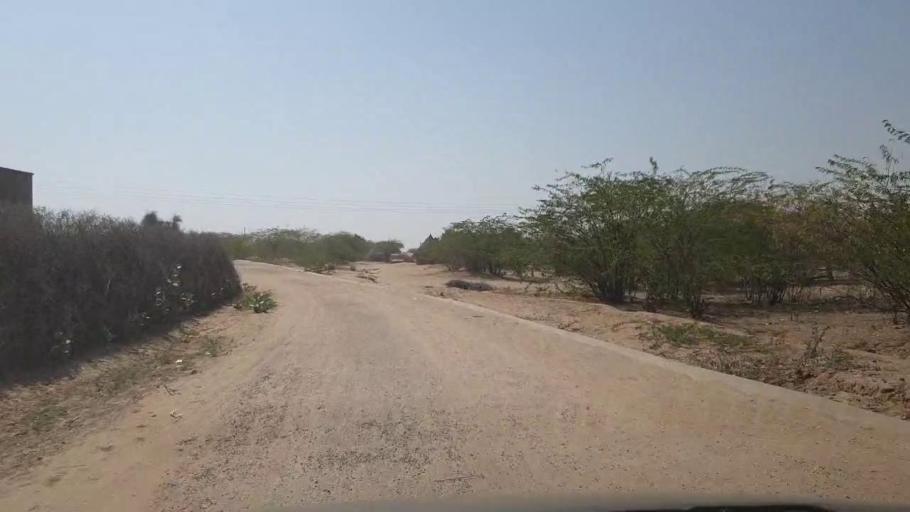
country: PK
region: Sindh
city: Chor
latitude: 25.5649
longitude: 70.1800
